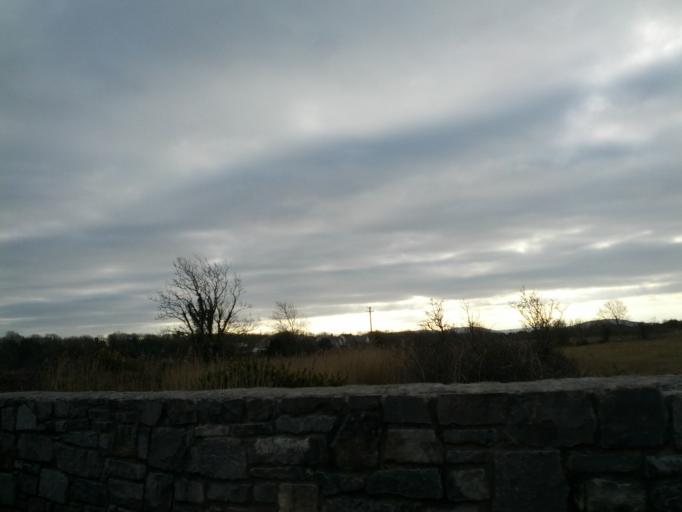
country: IE
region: Connaught
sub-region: County Galway
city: Oranmore
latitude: 53.1920
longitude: -8.9226
